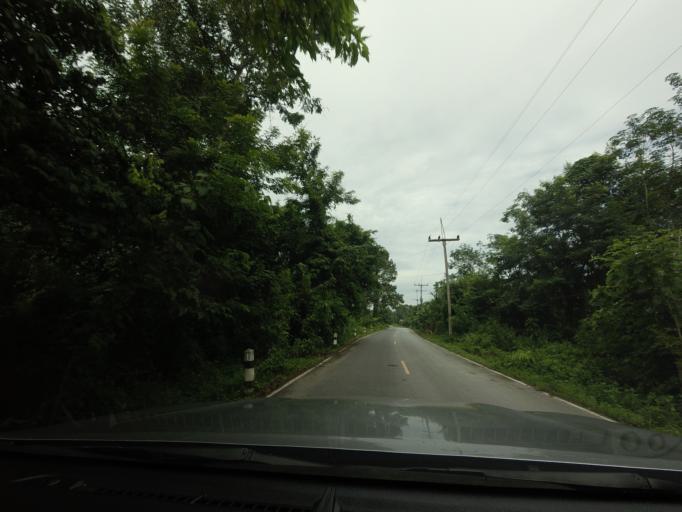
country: TH
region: Nakhon Si Thammarat
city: Phra Phrom
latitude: 8.2829
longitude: 99.9271
